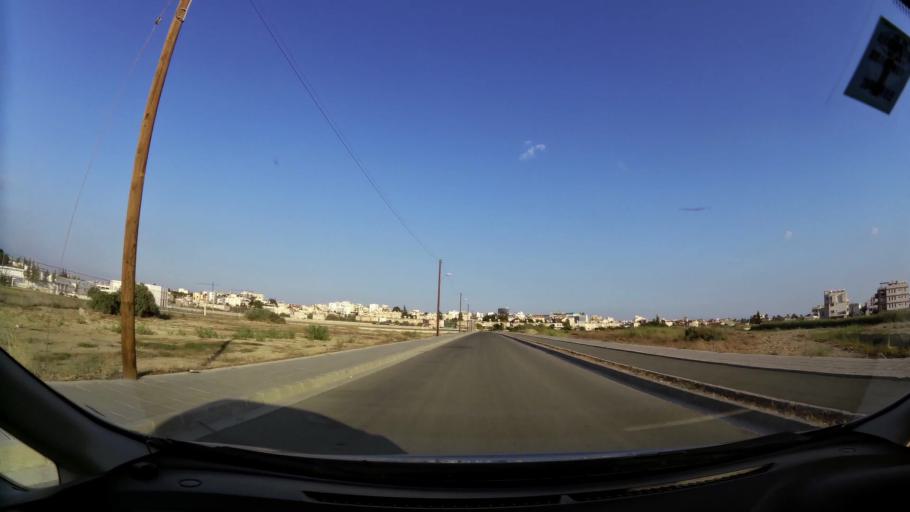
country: CY
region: Larnaka
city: Larnaca
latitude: 34.9182
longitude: 33.5941
